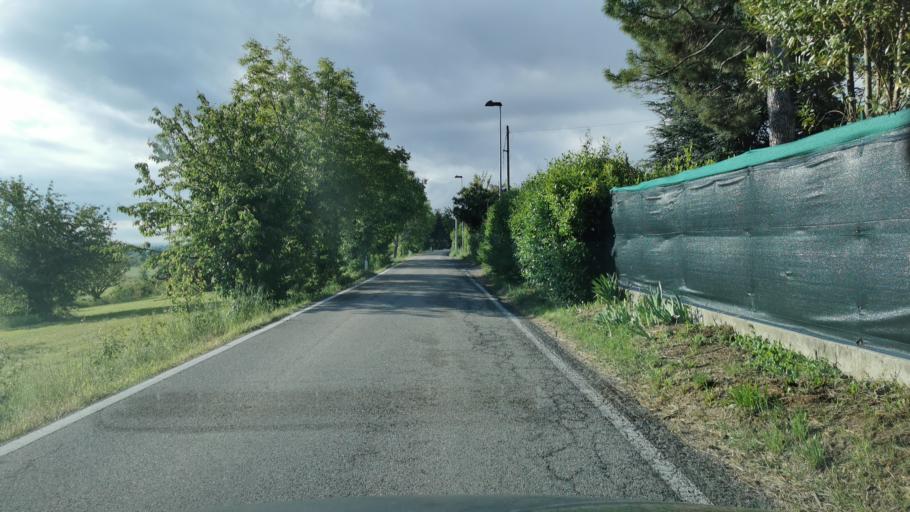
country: IT
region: Piedmont
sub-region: Provincia di Torino
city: Pino Torinese
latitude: 45.0194
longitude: 7.7762
